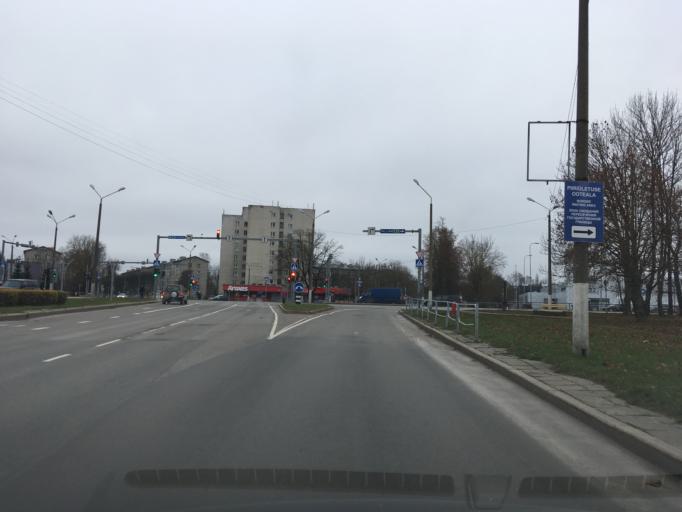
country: EE
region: Ida-Virumaa
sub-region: Narva linn
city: Narva
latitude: 59.3804
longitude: 28.1792
